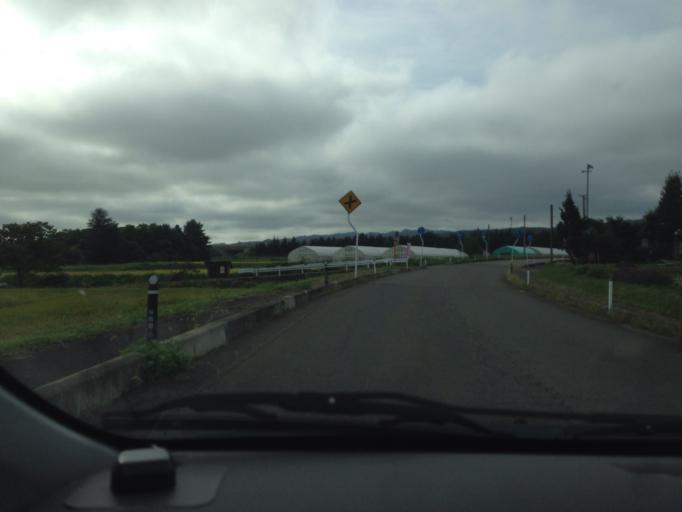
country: JP
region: Fukushima
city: Kitakata
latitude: 37.5455
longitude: 139.7995
